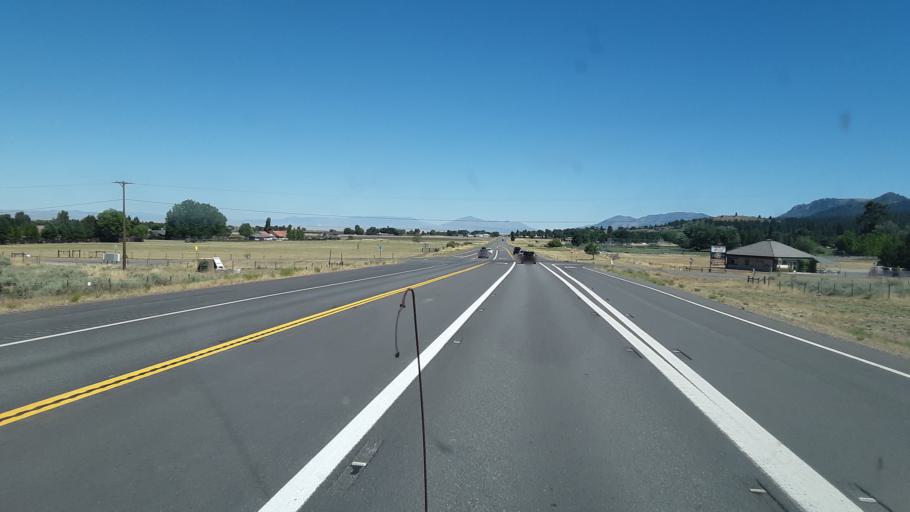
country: US
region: California
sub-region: Lassen County
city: Janesville
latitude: 40.3036
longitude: -120.5253
